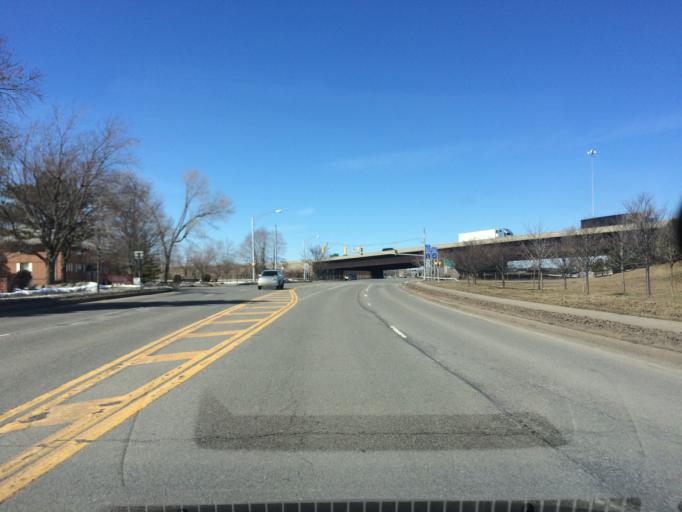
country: US
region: New York
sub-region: Monroe County
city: Brighton
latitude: 43.1419
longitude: -77.5467
